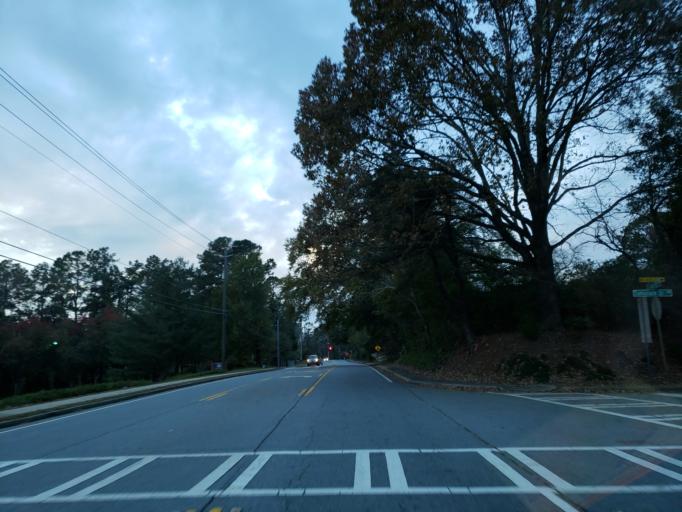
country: US
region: Georgia
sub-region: Cobb County
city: Acworth
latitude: 34.0155
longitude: -84.6727
